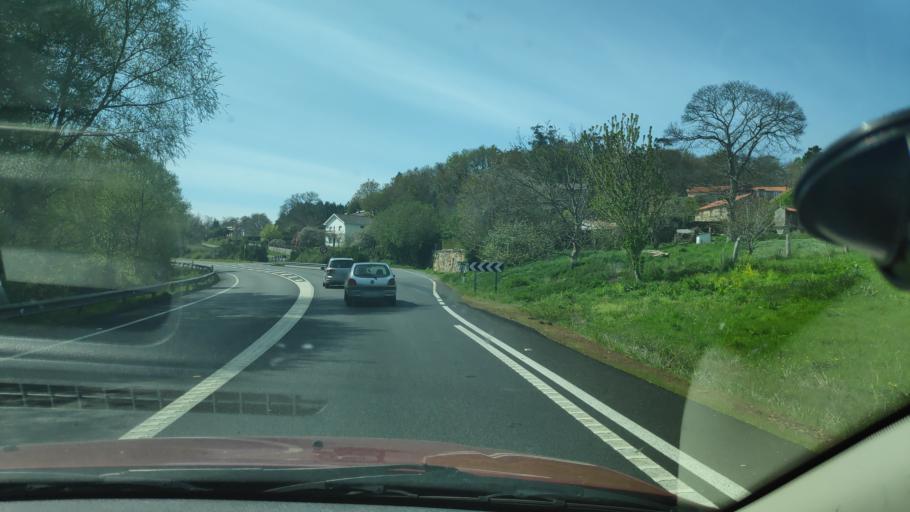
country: ES
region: Galicia
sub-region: Provincia da Coruna
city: Negreira
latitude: 42.8995
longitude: -8.6945
